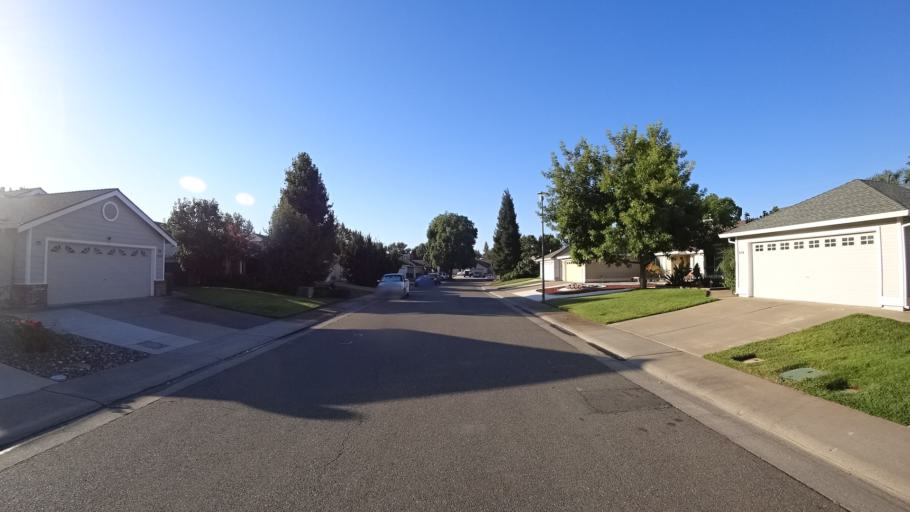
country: US
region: California
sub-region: Sacramento County
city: Laguna
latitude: 38.4251
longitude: -121.4542
